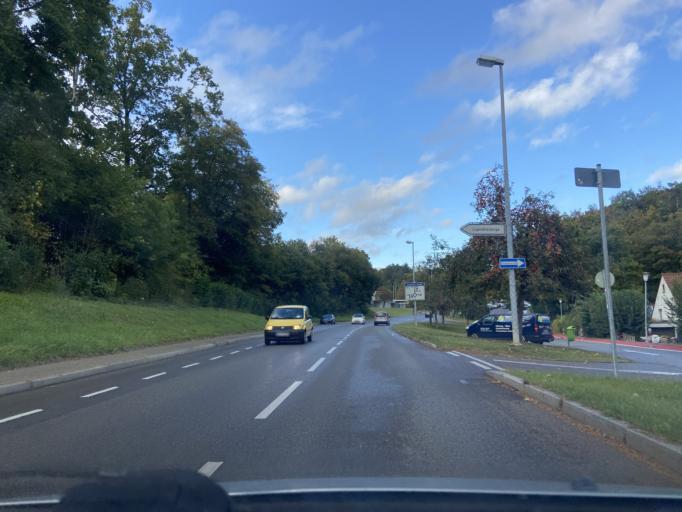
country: DE
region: Baden-Wuerttemberg
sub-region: Tuebingen Region
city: Sigmaringen
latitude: 48.0942
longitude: 9.2224
